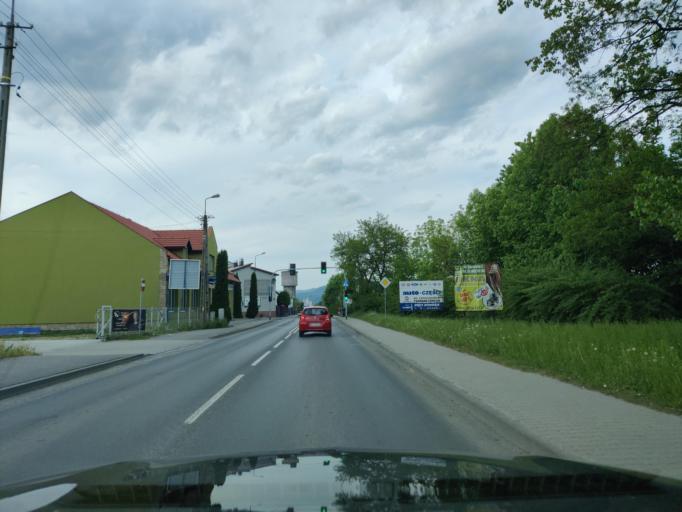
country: PL
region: Silesian Voivodeship
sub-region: Powiat zywiecki
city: Zywiec
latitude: 49.6780
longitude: 19.1836
